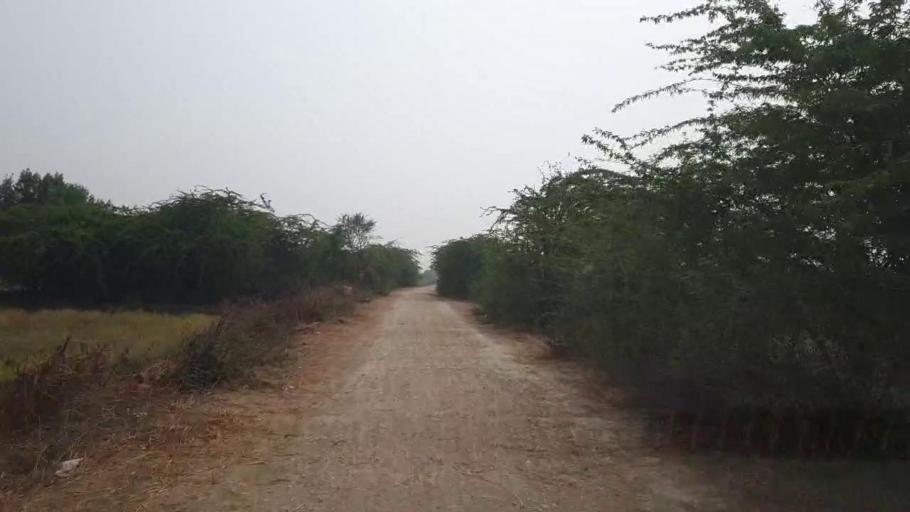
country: PK
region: Sindh
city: Kario
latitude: 24.6495
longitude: 68.6096
